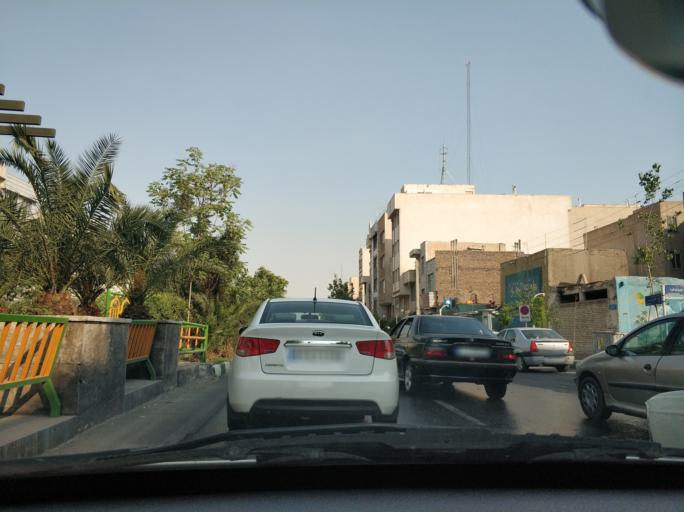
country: IR
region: Tehran
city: Tehran
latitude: 35.7280
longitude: 51.4674
